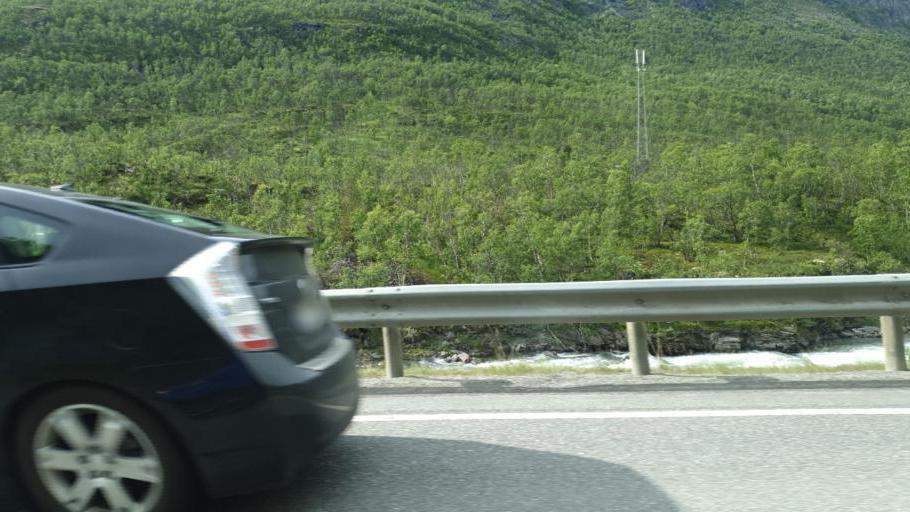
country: NO
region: Sor-Trondelag
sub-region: Oppdal
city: Oppdal
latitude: 62.3184
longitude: 9.6204
